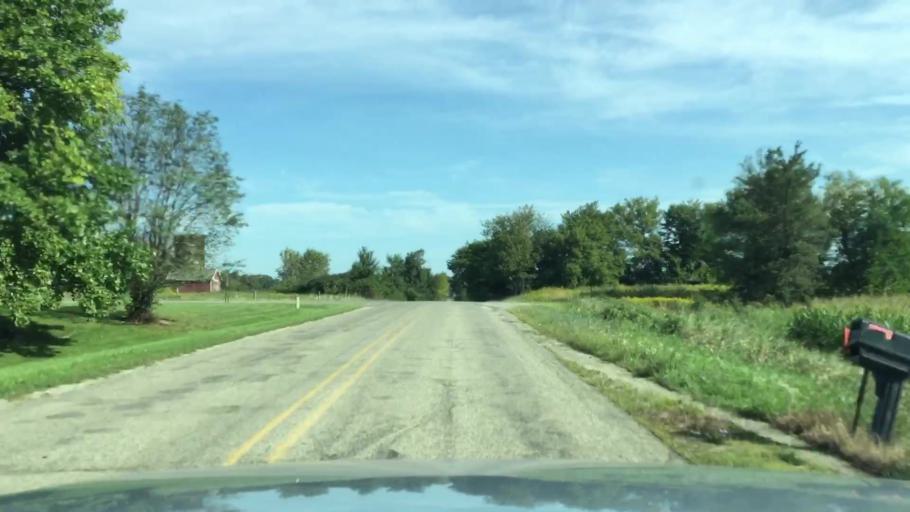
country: US
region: Michigan
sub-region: Lenawee County
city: Hudson
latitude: 41.9125
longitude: -84.4205
